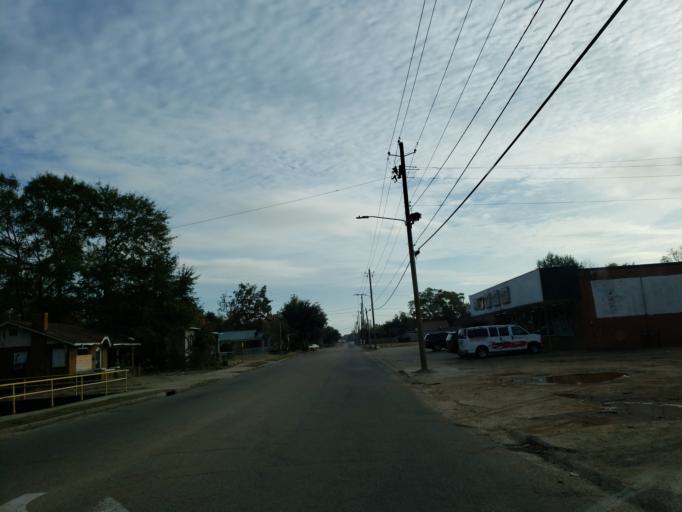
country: US
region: Mississippi
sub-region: Forrest County
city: Hattiesburg
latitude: 31.3147
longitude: -89.2851
